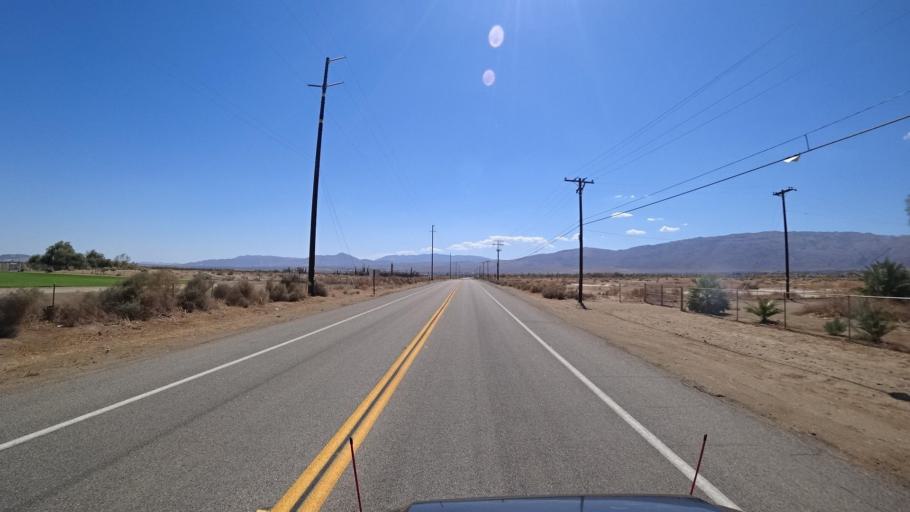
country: US
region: California
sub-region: San Diego County
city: Borrego Springs
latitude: 33.2554
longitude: -116.3480
